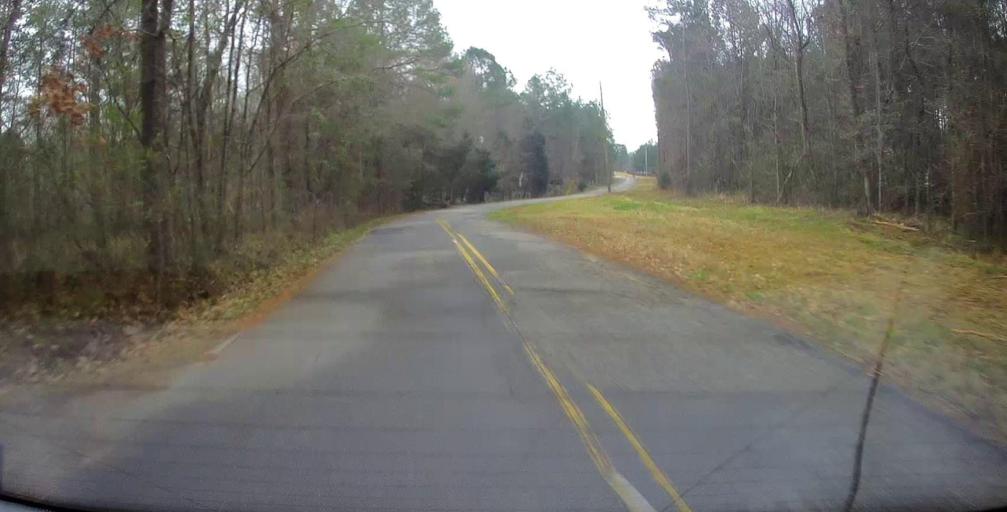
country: US
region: Georgia
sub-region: Monroe County
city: Forsyth
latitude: 33.0110
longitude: -83.8218
